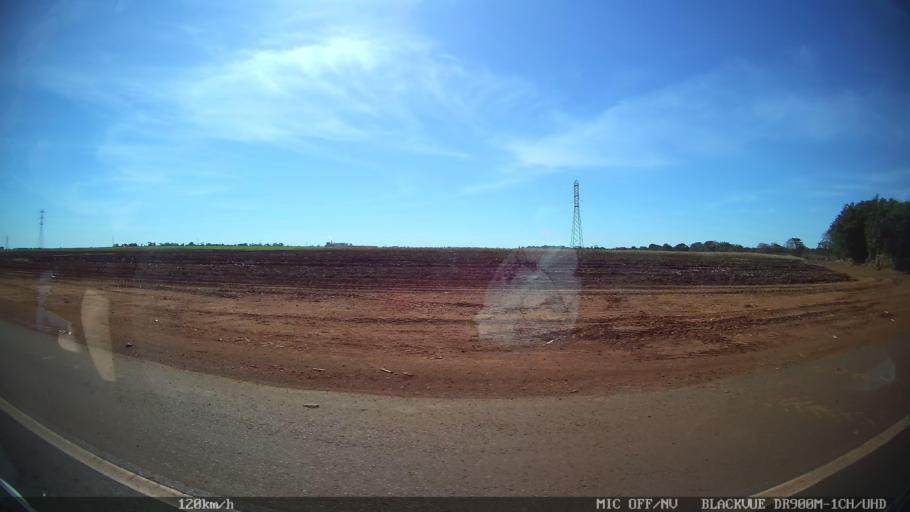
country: BR
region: Sao Paulo
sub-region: Guaira
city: Guaira
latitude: -20.4471
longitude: -48.2061
